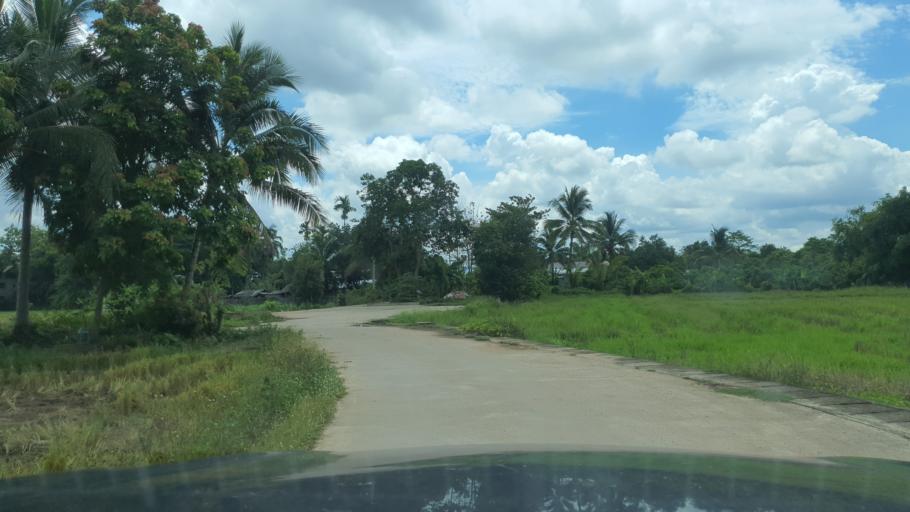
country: TH
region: Chiang Mai
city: San Sai
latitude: 18.8790
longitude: 99.0498
